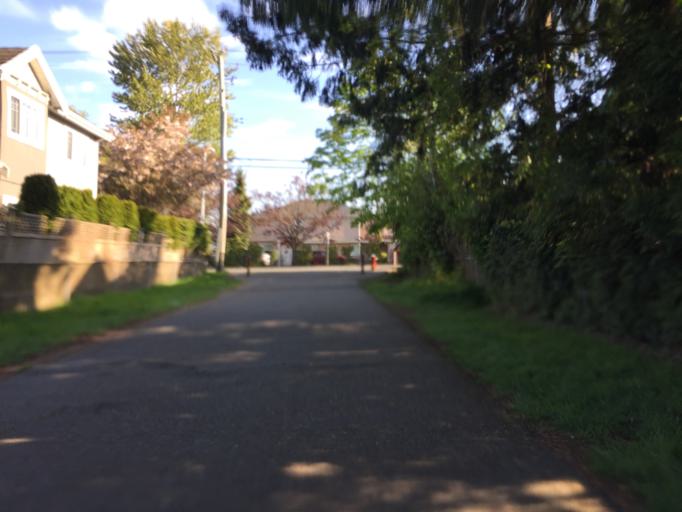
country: CA
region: British Columbia
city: Richmond
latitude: 49.1552
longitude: -123.1449
